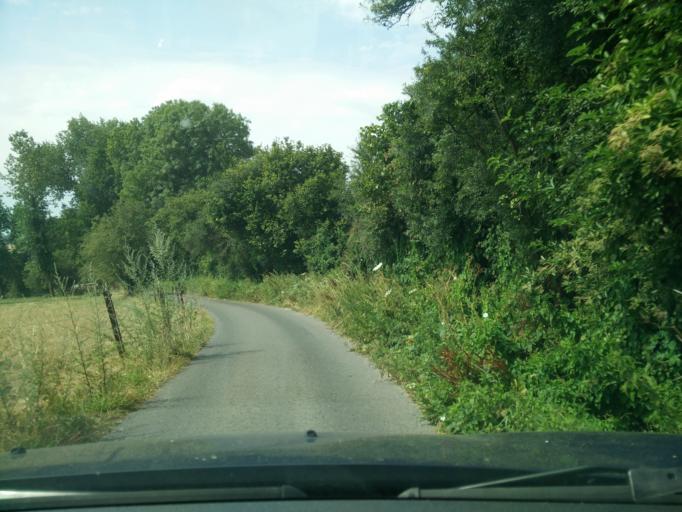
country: BE
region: Wallonia
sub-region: Province du Brabant Wallon
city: Tubize
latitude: 50.6998
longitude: 4.2318
